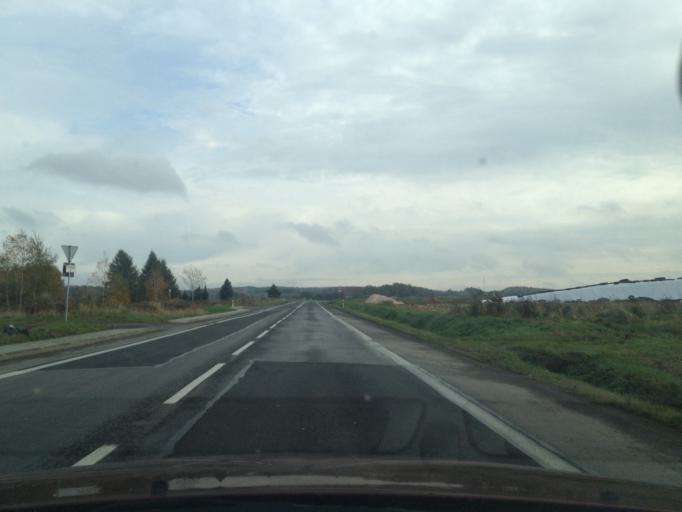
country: PL
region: Lower Silesian Voivodeship
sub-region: Powiat zgorzelecki
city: Lagow
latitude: 51.1553
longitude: 15.1082
